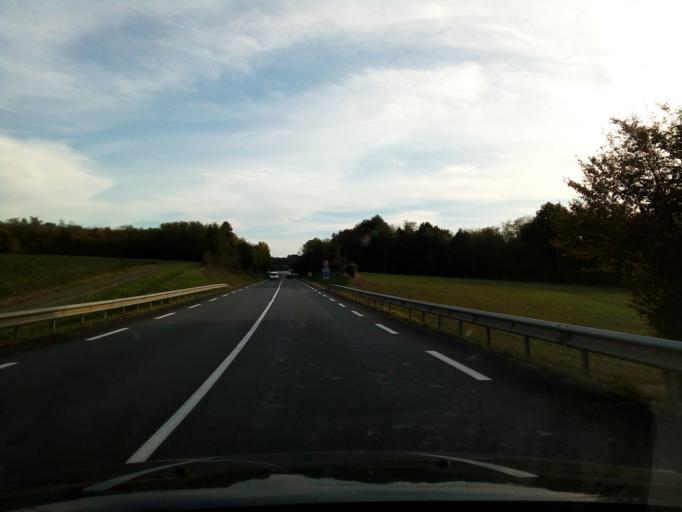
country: FR
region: Poitou-Charentes
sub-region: Departement de la Charente
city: Saint-Claud
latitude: 45.8661
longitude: 0.4657
